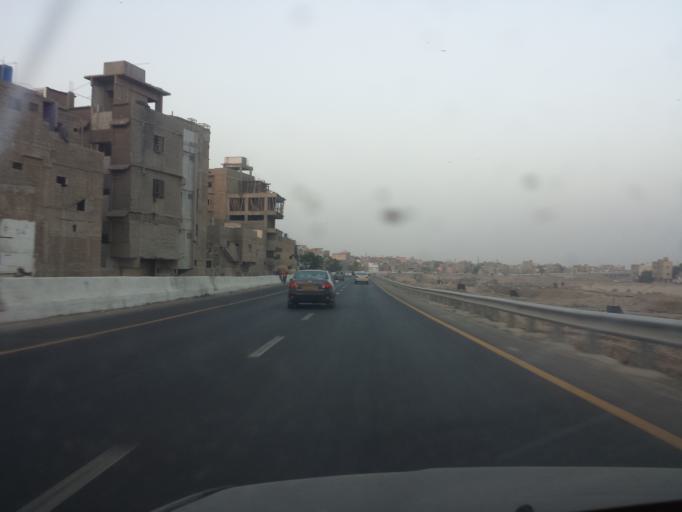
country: PK
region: Sindh
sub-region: Karachi District
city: Karachi
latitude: 24.8917
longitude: 67.0339
